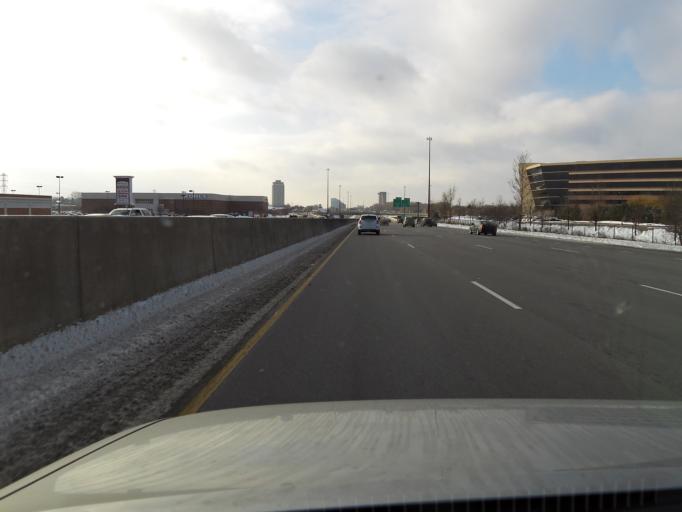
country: US
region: Minnesota
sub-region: Hennepin County
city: Bloomington
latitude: 44.8619
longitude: -93.3026
